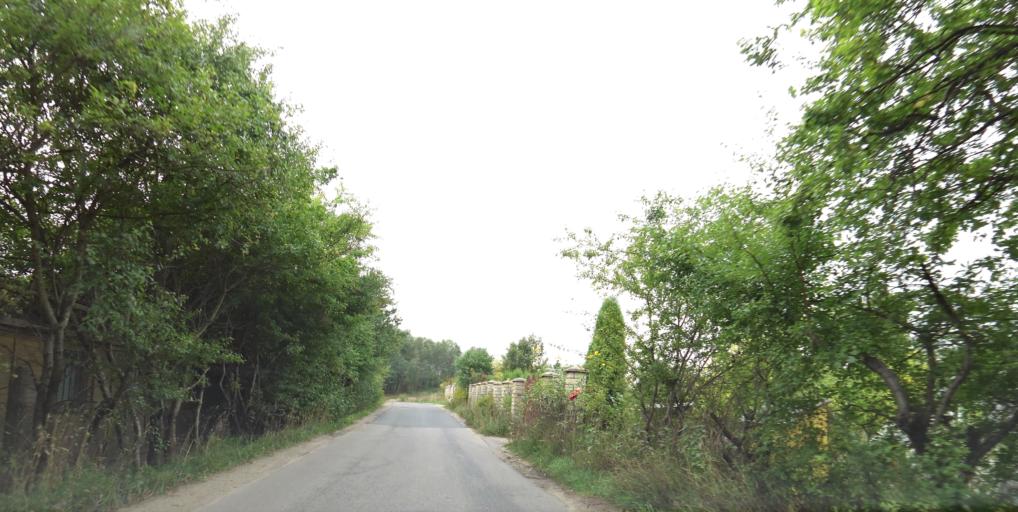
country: LT
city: Grigiskes
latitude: 54.7609
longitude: 25.0397
